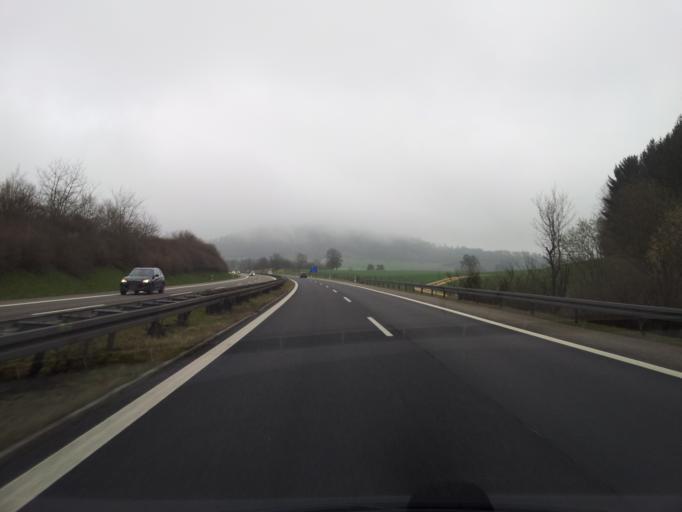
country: DE
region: Baden-Wuerttemberg
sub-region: Freiburg Region
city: Hilzingen
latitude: 47.7539
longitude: 8.7806
